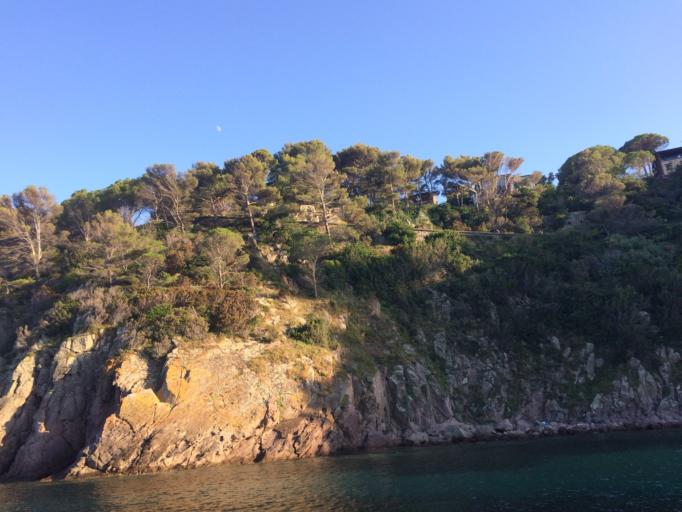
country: IT
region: Tuscany
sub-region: Provincia di Livorno
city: Capraia Isola
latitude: 43.0498
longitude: 9.8391
